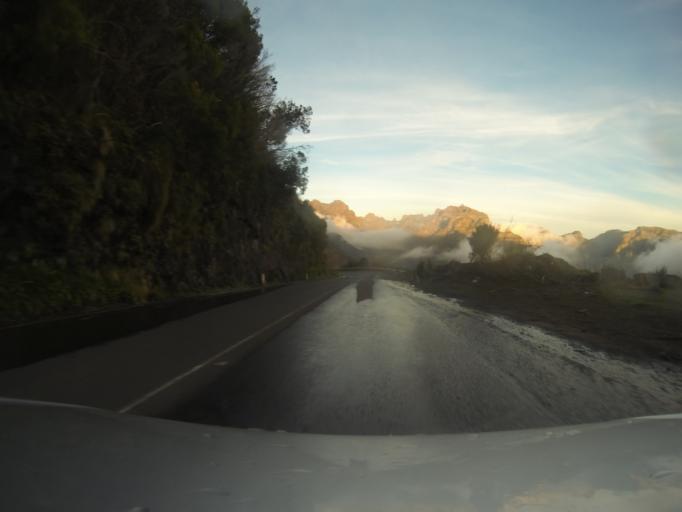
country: PT
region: Madeira
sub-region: Sao Vicente
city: Sao Vicente
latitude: 32.7502
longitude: -17.0310
